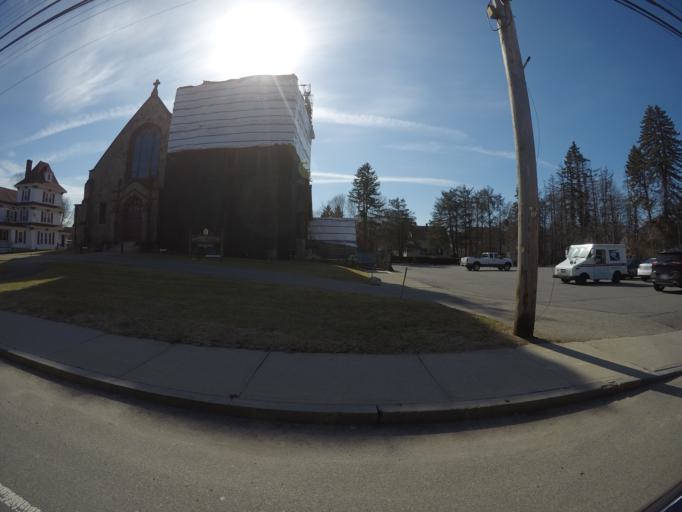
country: US
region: Massachusetts
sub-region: Bristol County
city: Easton
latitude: 42.0658
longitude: -71.0993
